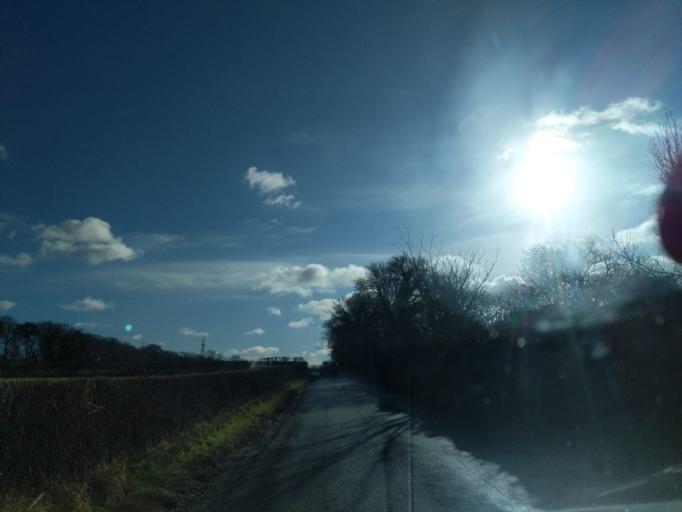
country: GB
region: Scotland
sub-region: East Lothian
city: Haddington
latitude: 55.9577
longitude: -2.7460
